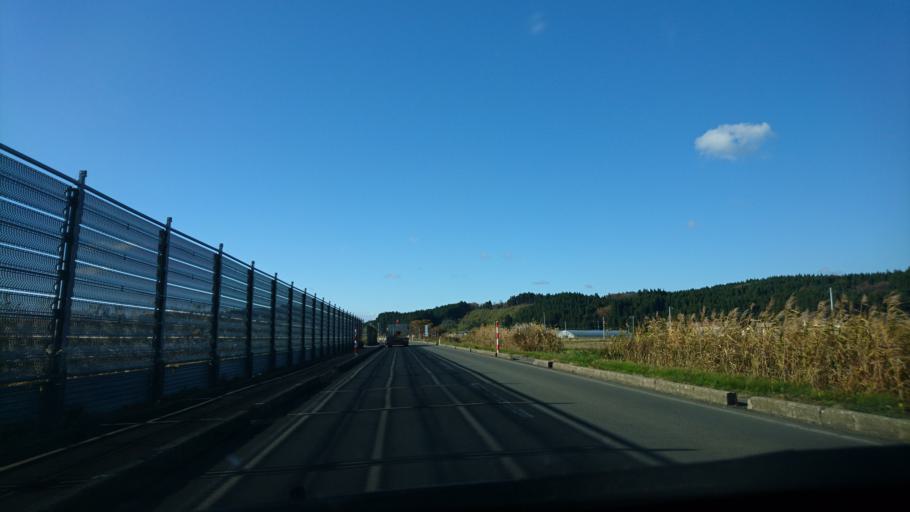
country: JP
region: Akita
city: Akita
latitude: 39.3467
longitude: 140.1146
